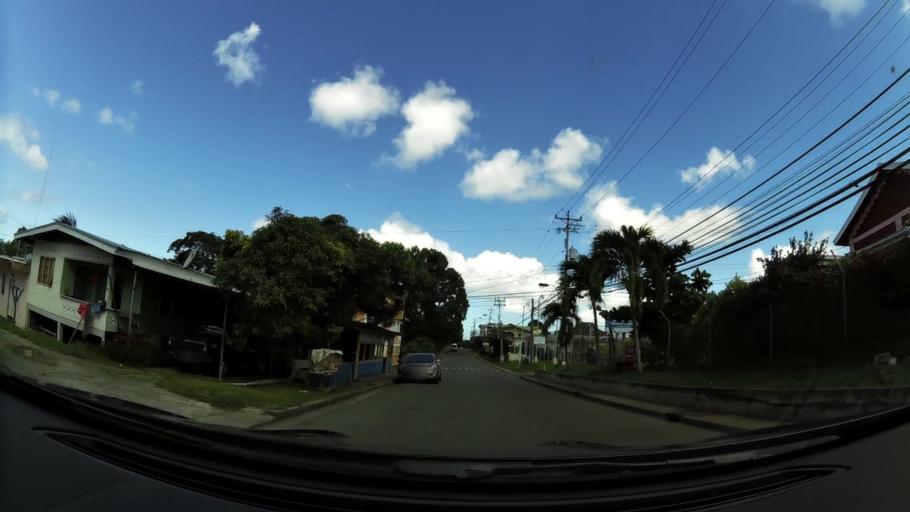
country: TT
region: Tobago
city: Scarborough
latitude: 11.2052
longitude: -60.7812
